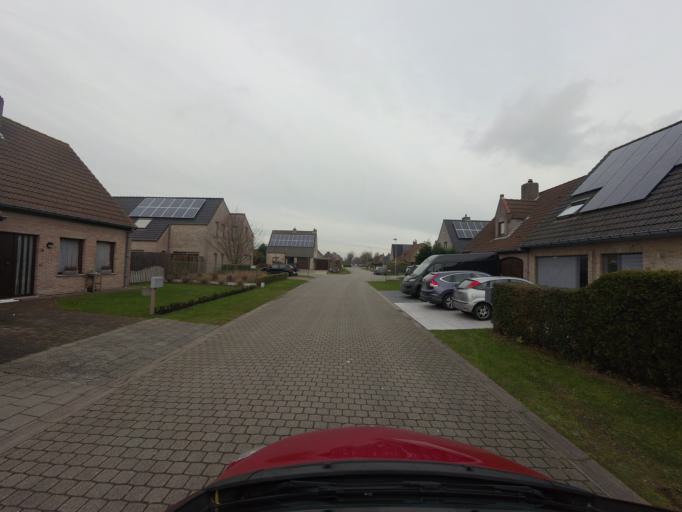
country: BE
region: Flanders
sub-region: Provincie West-Vlaanderen
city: Bredene
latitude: 51.2339
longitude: 2.9660
